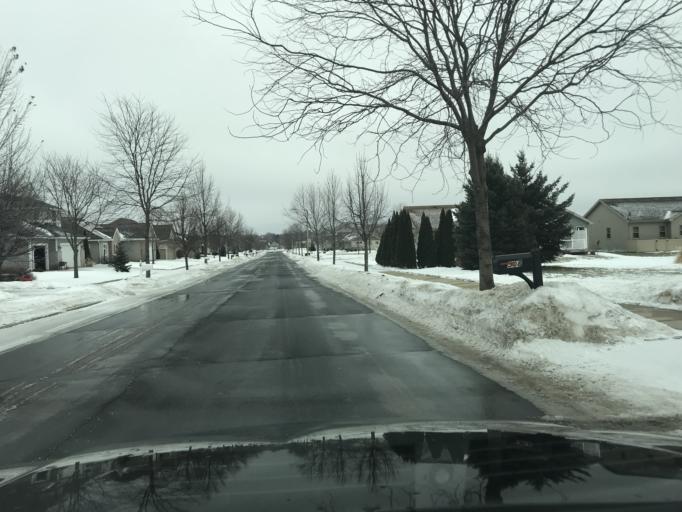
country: US
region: Wisconsin
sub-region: Dane County
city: Cottage Grove
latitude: 43.0932
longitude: -89.2158
